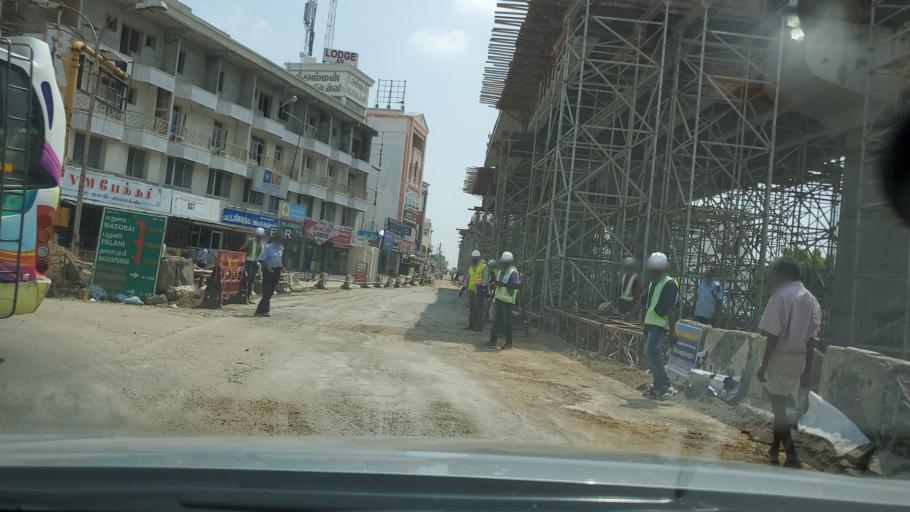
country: IN
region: Tamil Nadu
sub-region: Tiruppur
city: Dharapuram
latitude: 10.7356
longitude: 77.5175
